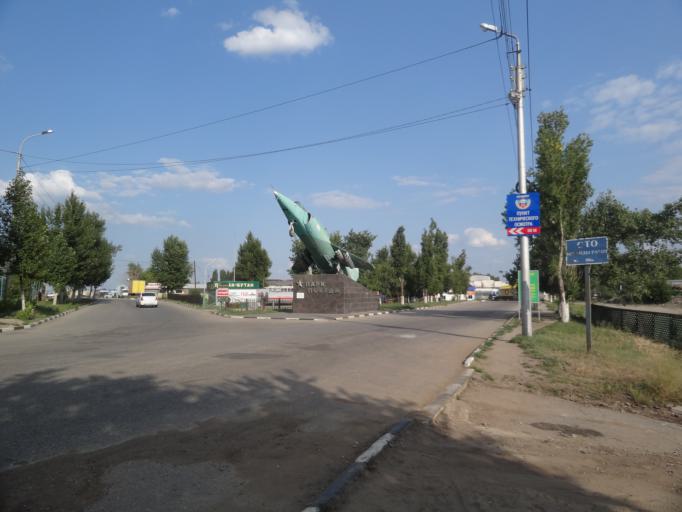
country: RU
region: Saratov
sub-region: Saratovskiy Rayon
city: Saratov
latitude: 51.5501
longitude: 46.0523
